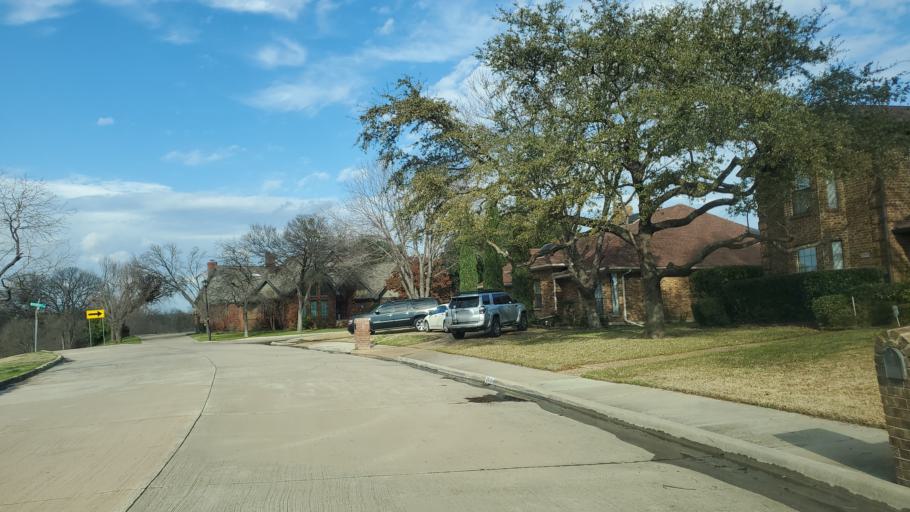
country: US
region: Texas
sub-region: Dallas County
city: Carrollton
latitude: 32.9950
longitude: -96.8937
